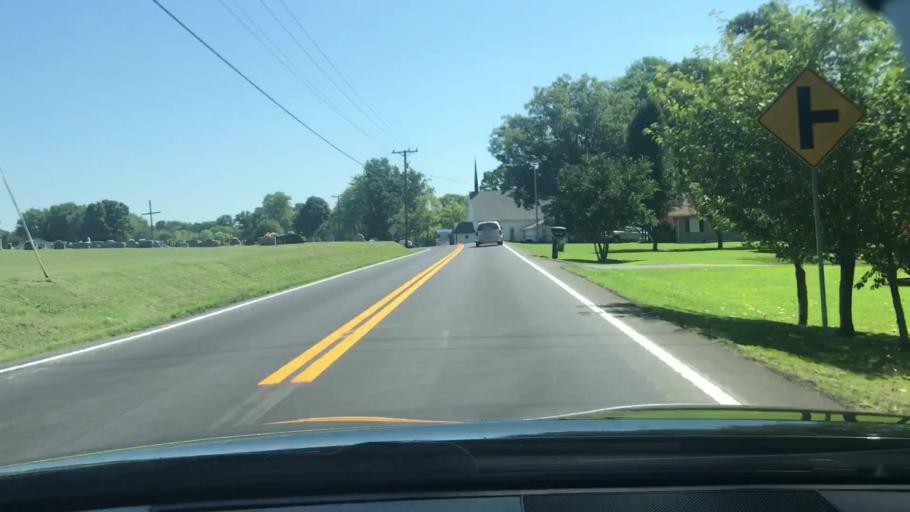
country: US
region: Tennessee
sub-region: Sumner County
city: White House
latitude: 36.4842
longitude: -86.6128
